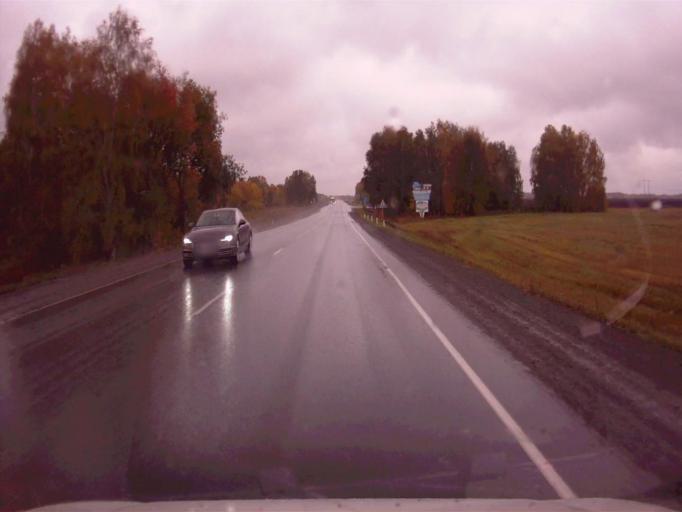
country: RU
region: Chelyabinsk
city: Roshchino
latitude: 55.3947
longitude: 61.1016
